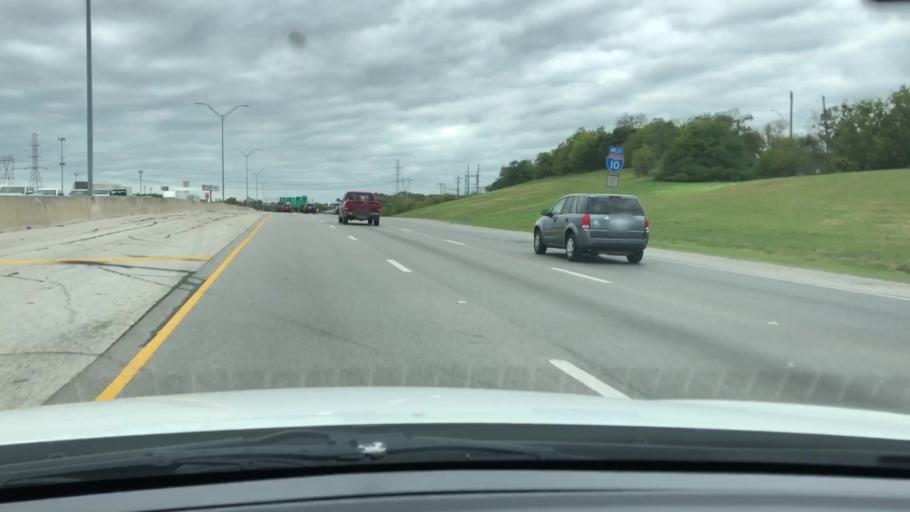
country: US
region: Texas
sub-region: Bexar County
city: San Antonio
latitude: 29.4077
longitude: -98.4383
